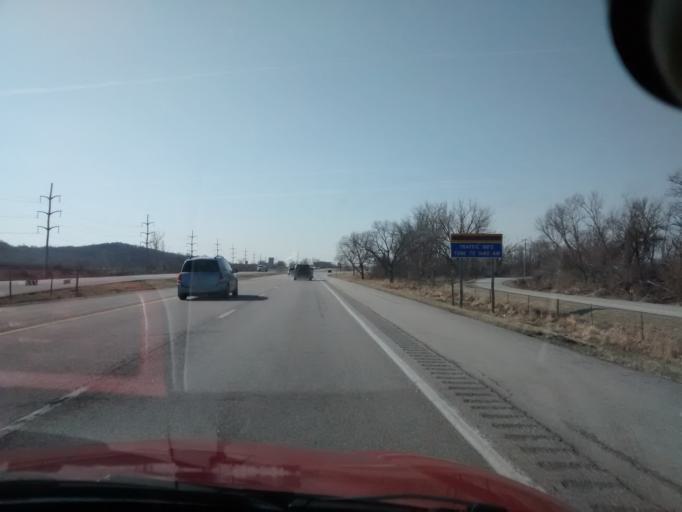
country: US
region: Iowa
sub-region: Pottawattamie County
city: Council Bluffs
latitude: 41.2989
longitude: -95.8679
